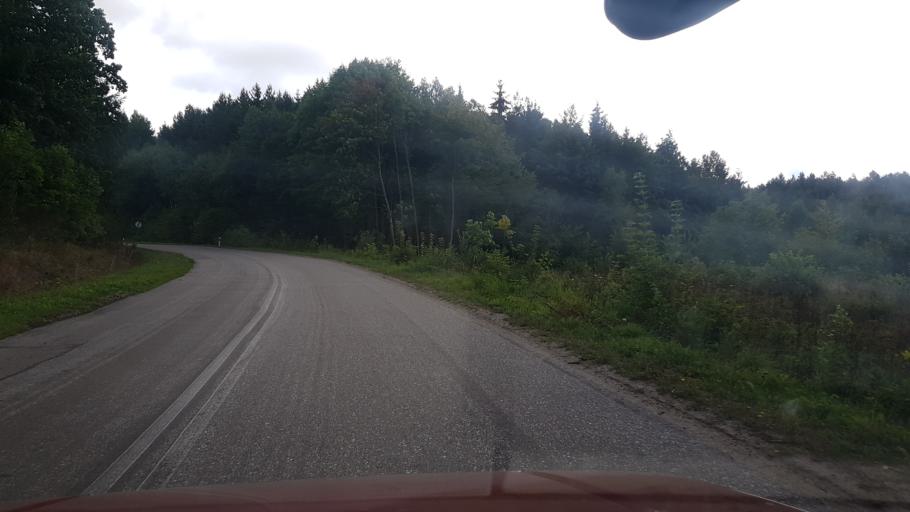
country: PL
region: West Pomeranian Voivodeship
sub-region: Powiat koszalinski
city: Polanow
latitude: 54.0892
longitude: 16.8357
